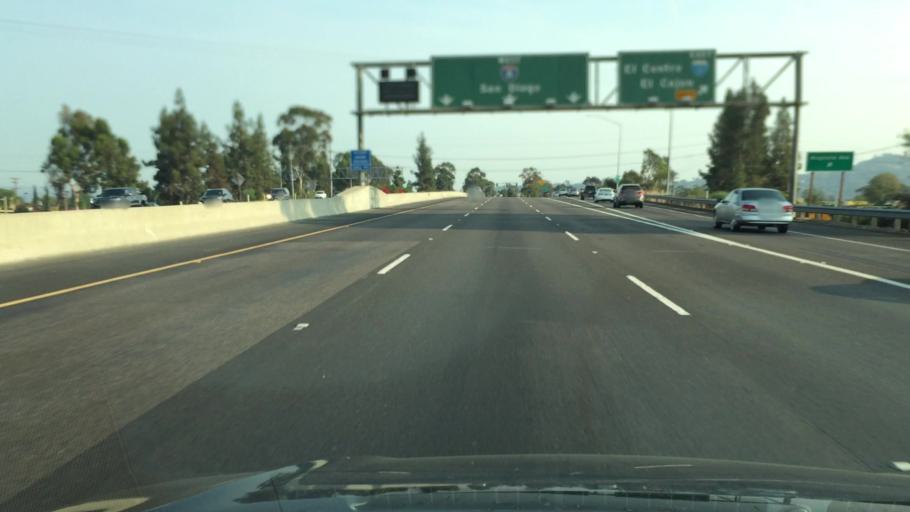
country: US
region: California
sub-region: San Diego County
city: El Cajon
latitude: 32.8100
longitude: -116.9620
